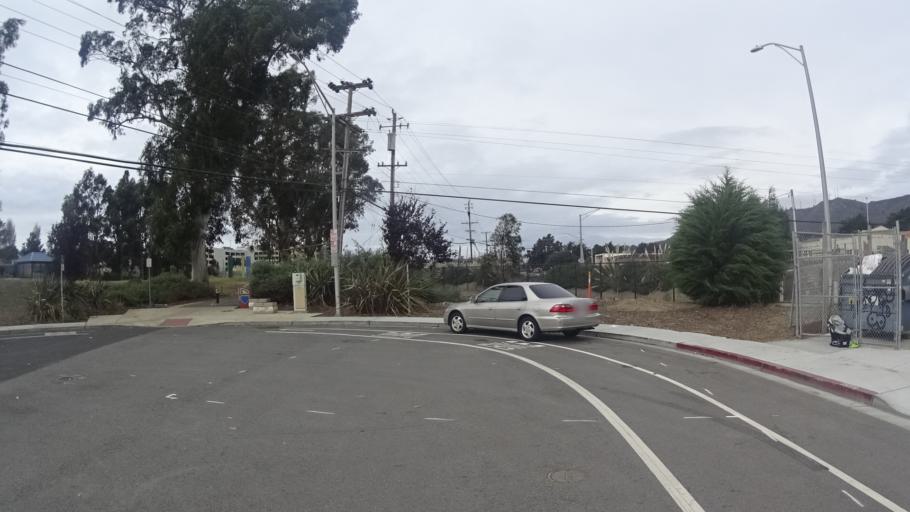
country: US
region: California
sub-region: San Mateo County
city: South San Francisco
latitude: 37.6572
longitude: -122.4346
